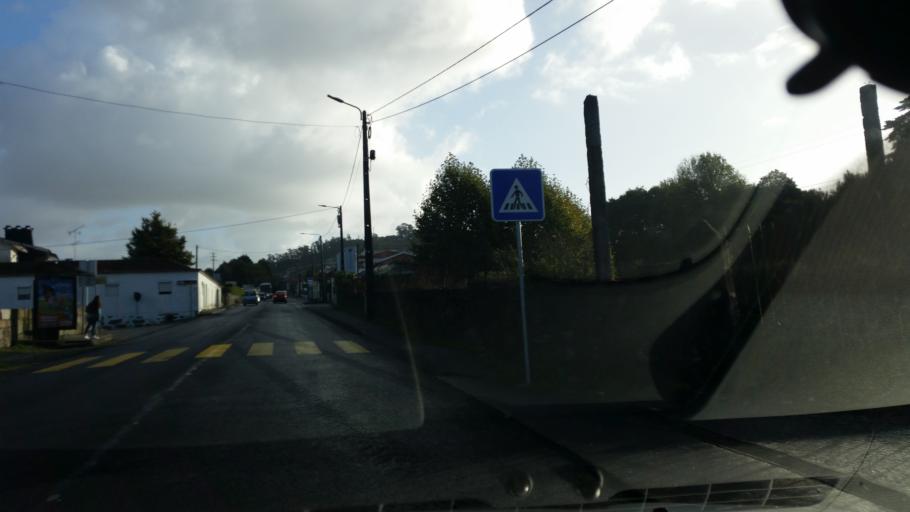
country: PT
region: Porto
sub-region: Santo Tirso
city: Sao Miguel do Couto
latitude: 41.3482
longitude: -8.4590
